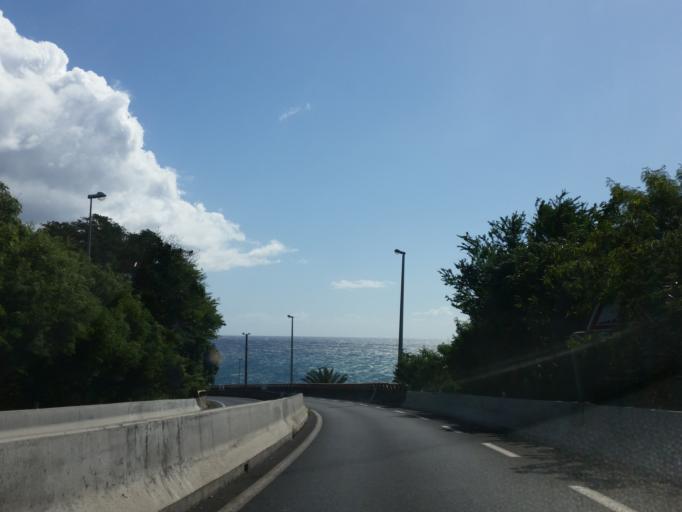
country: RE
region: Reunion
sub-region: Reunion
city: Saint-Denis
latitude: -20.8774
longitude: 55.4375
